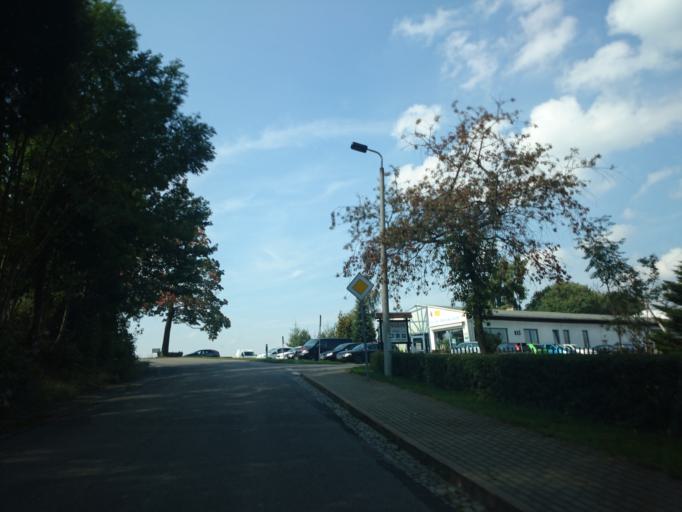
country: DE
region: Saxony
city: Brand-Erbisdorf
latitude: 50.8343
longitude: 13.2941
